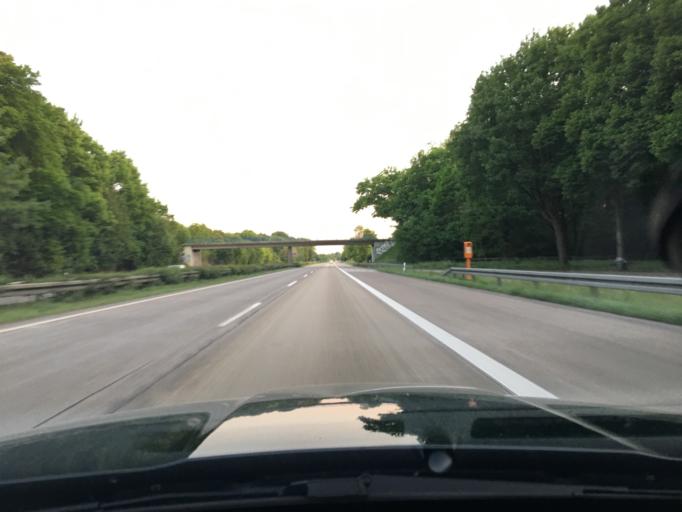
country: DE
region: North Rhine-Westphalia
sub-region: Regierungsbezirk Munster
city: Ladbergen
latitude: 52.1379
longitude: 7.7250
